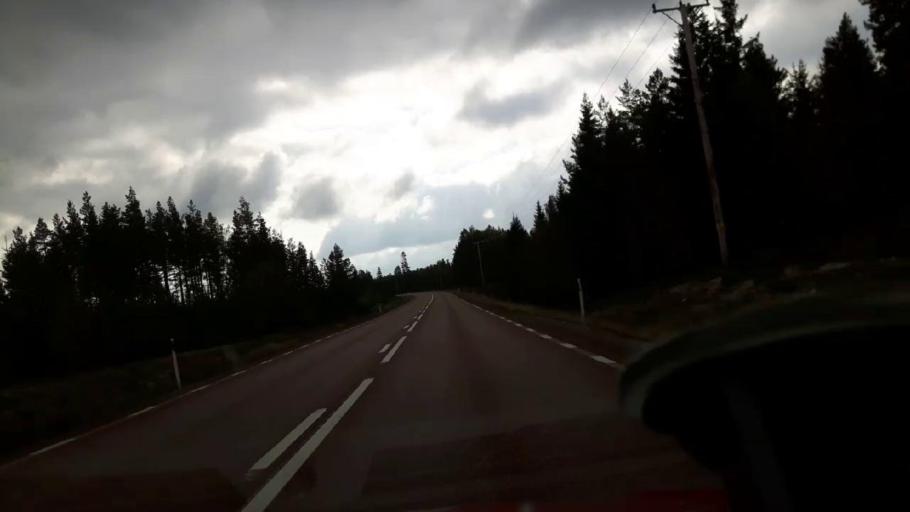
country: SE
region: Gaevleborg
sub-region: Soderhamns Kommun
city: Ljusne
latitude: 61.1161
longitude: 16.9350
